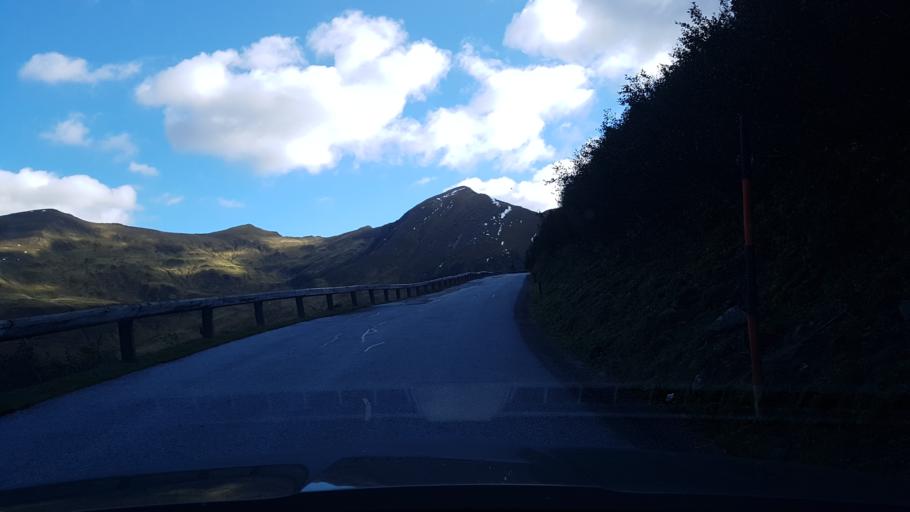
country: AT
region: Styria
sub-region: Politischer Bezirk Liezen
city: Sankt Nikolai im Solktal
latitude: 47.2746
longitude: 14.0805
